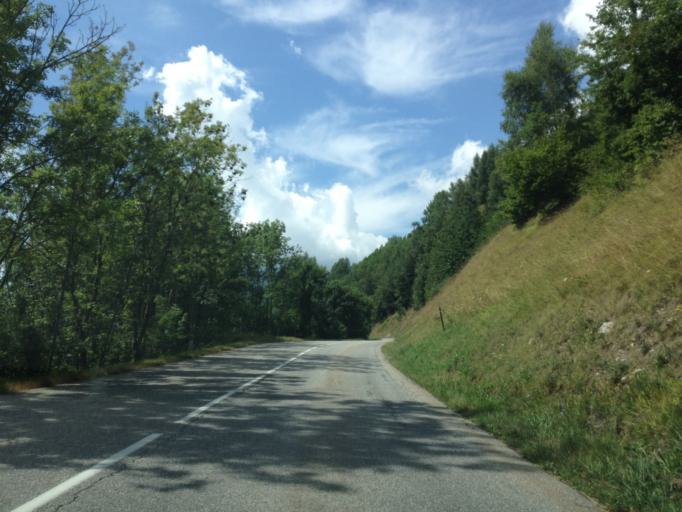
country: FR
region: Rhone-Alpes
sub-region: Departement de la Savoie
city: Salins-les-Thermes
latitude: 45.4483
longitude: 6.4974
